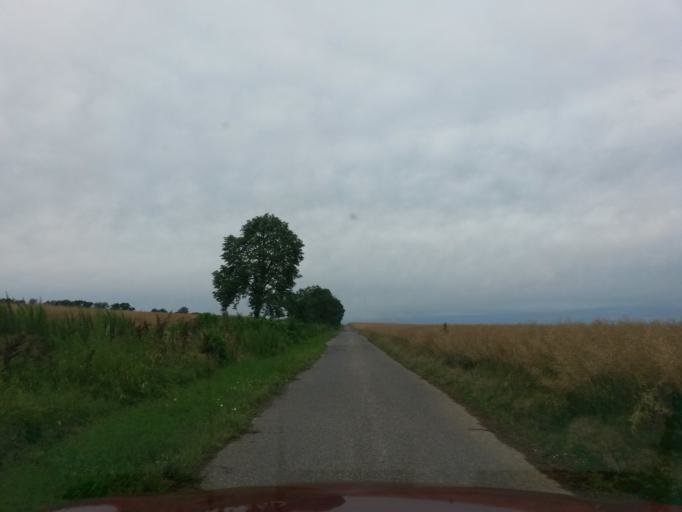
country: SK
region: Banskobystricky
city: Dudince
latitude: 48.1325
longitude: 18.8673
